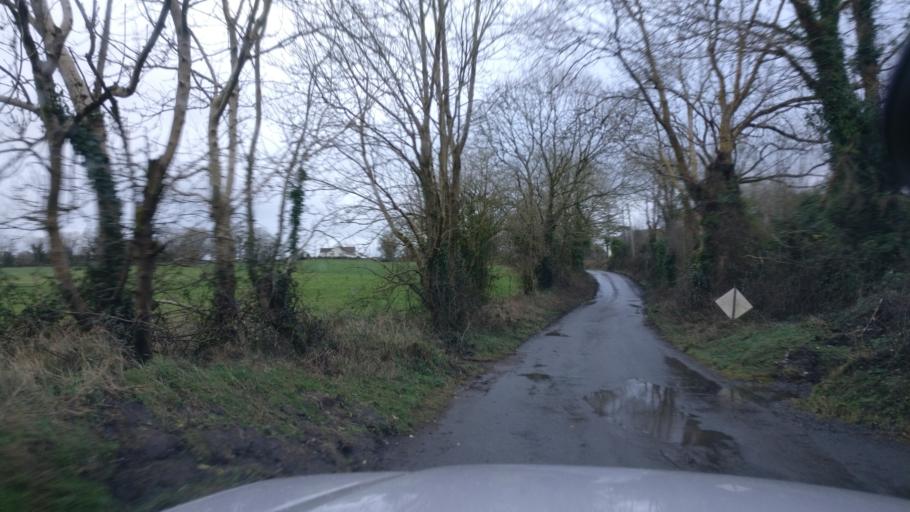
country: IE
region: Connaught
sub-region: County Galway
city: Athenry
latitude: 53.2108
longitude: -8.6968
